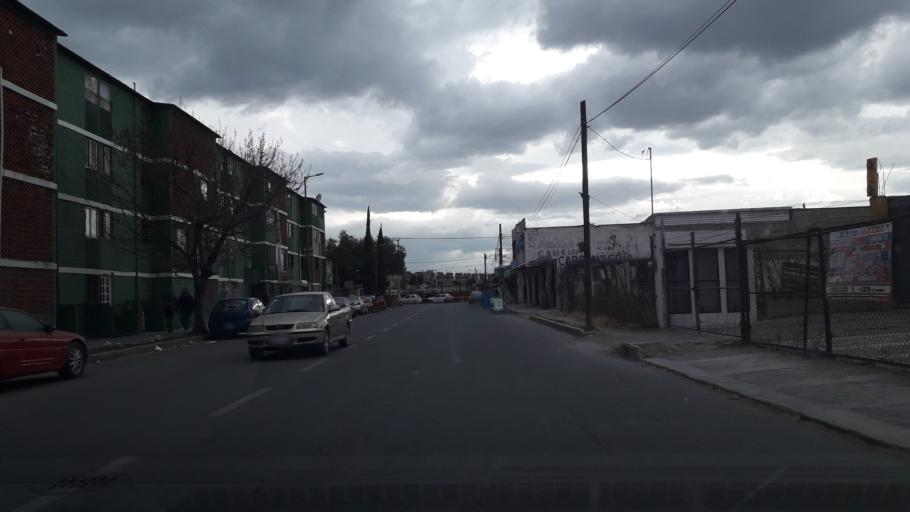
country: MX
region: Mexico
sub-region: Jaltenco
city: Alborada Jaltenco
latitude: 19.6649
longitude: -99.0695
